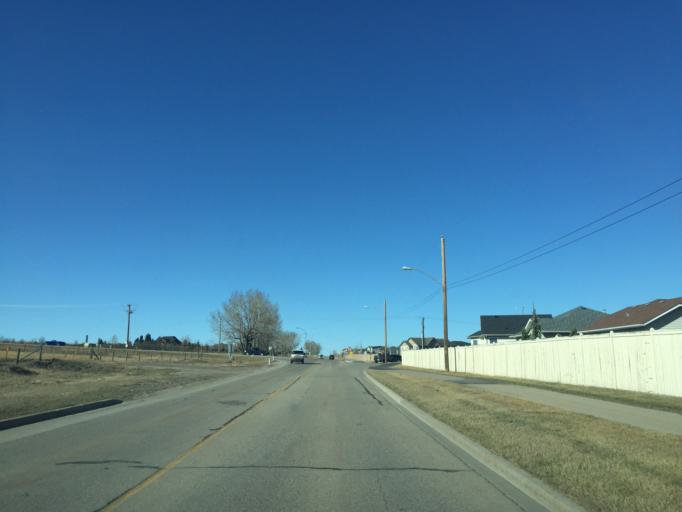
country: CA
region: Alberta
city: Airdrie
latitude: 51.2988
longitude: -114.0485
